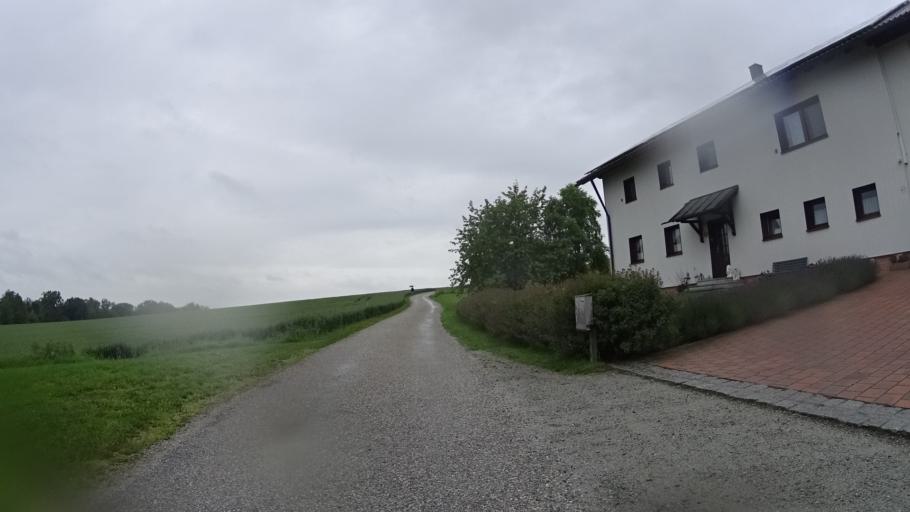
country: AT
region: Upper Austria
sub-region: Politischer Bezirk Scharding
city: Scharding
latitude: 48.4785
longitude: 13.4342
